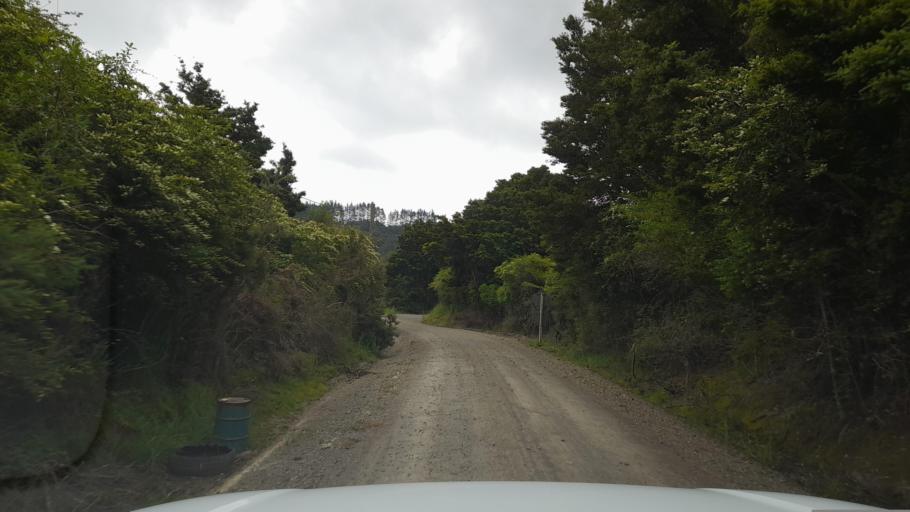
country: NZ
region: Northland
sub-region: Far North District
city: Waimate North
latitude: -35.3986
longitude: 173.7852
